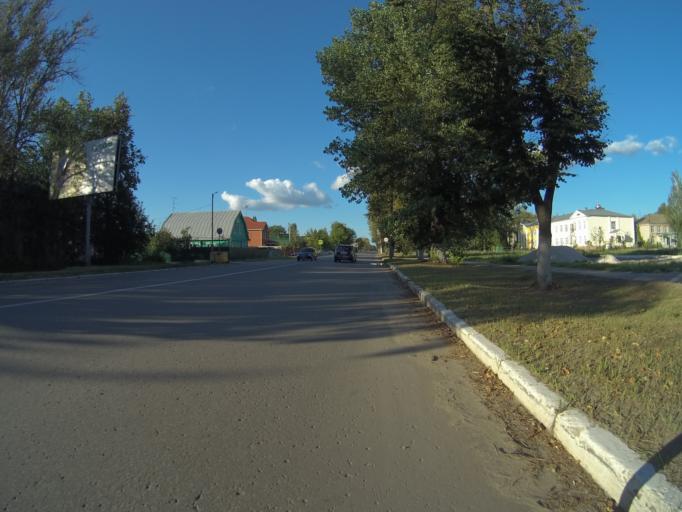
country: RU
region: Vladimir
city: Gus'-Khrustal'nyy
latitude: 55.6193
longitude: 40.6766
